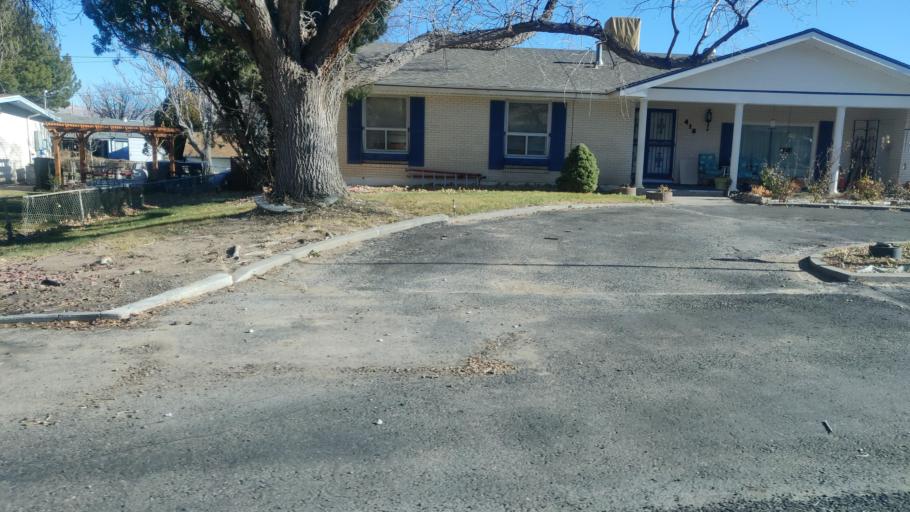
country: US
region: Colorado
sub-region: Mesa County
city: Grand Junction
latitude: 39.0659
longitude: -108.5933
